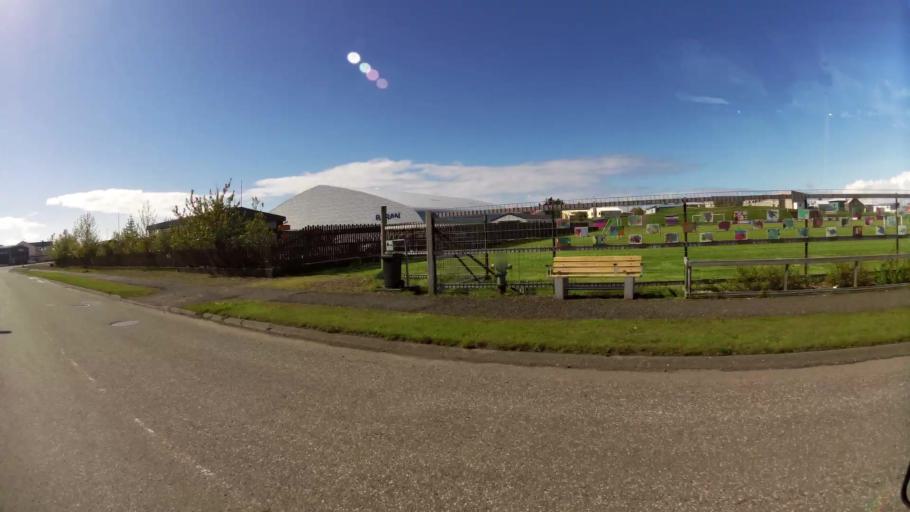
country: IS
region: East
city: Hoefn
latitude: 64.2528
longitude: -15.2042
